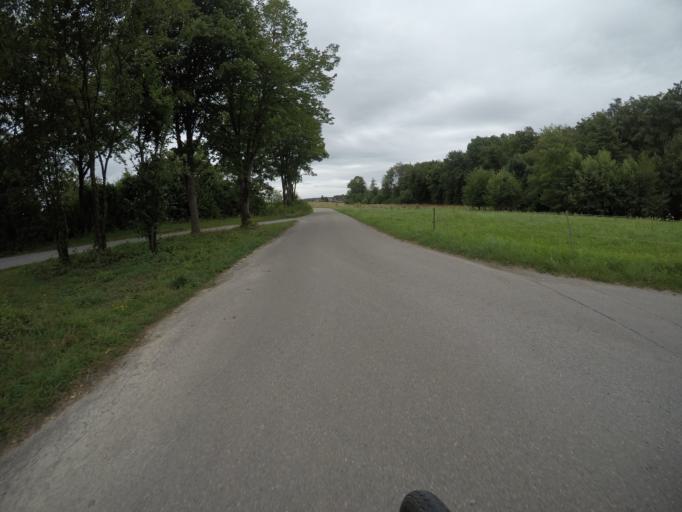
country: DE
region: Baden-Wuerttemberg
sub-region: Regierungsbezirk Stuttgart
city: Nufringen
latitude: 48.6176
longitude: 8.9145
